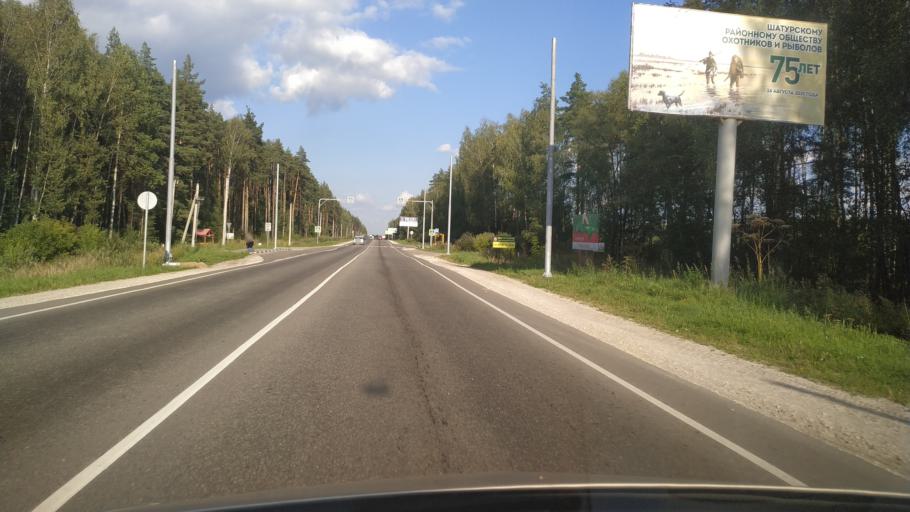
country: RU
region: Moskovskaya
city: Shaturtorf
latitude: 55.5782
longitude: 39.4365
